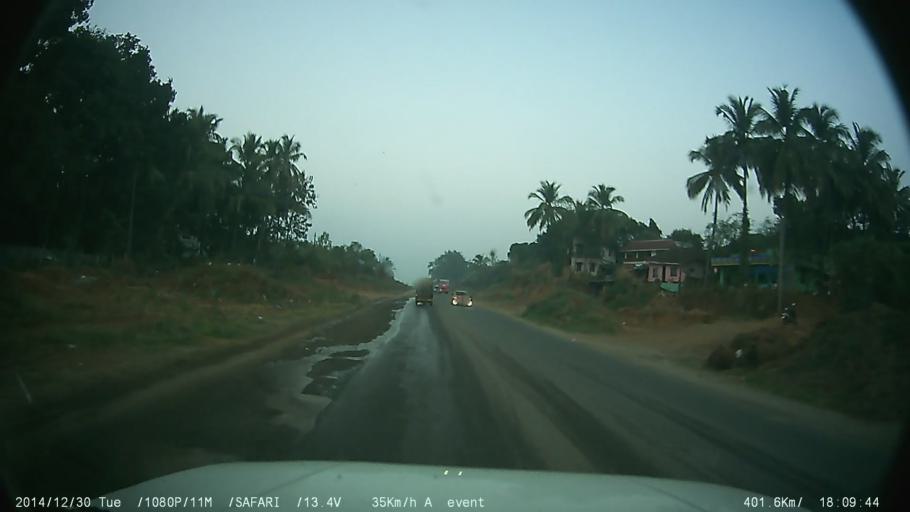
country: IN
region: Kerala
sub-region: Thrissur District
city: Chelakara
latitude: 10.6070
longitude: 76.4949
